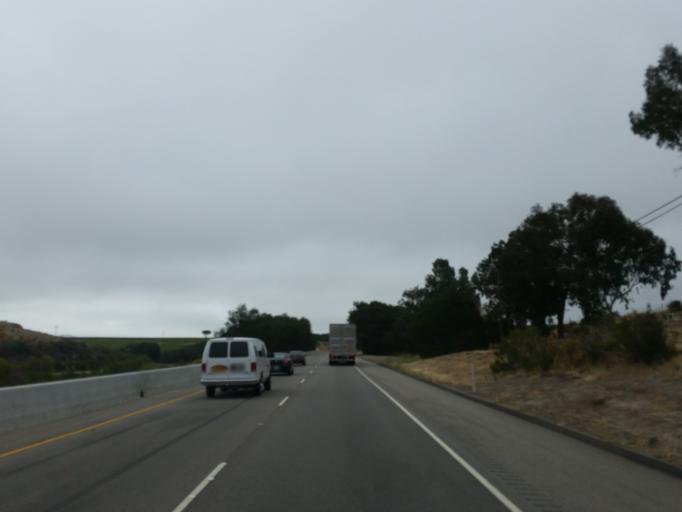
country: US
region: California
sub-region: San Luis Obispo County
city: Arroyo Grande
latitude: 35.0882
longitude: -120.5368
